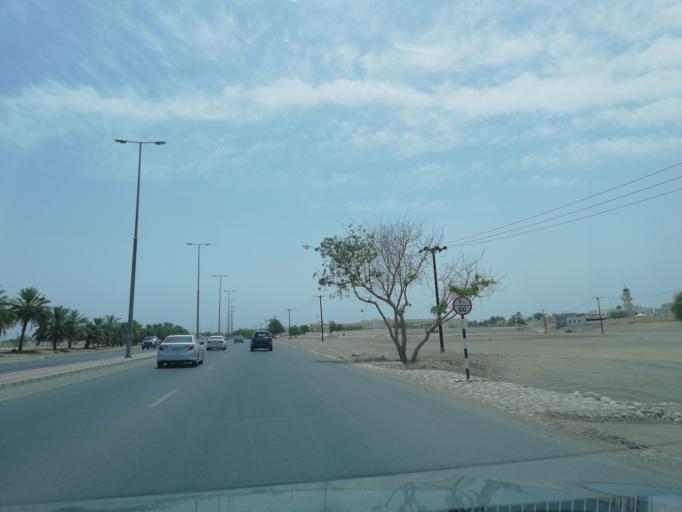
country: OM
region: Muhafazat Masqat
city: As Sib al Jadidah
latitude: 23.6744
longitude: 58.1654
